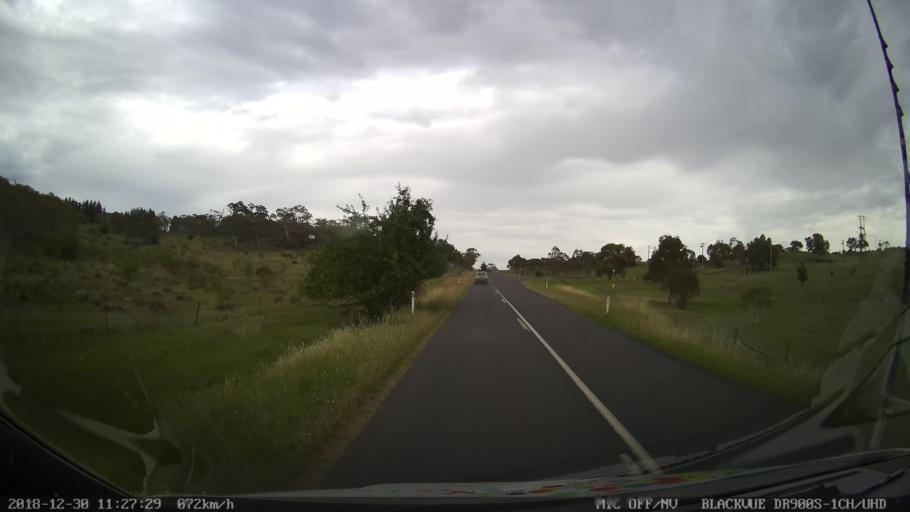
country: AU
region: New South Wales
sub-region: Snowy River
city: Jindabyne
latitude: -36.4603
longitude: 148.6265
